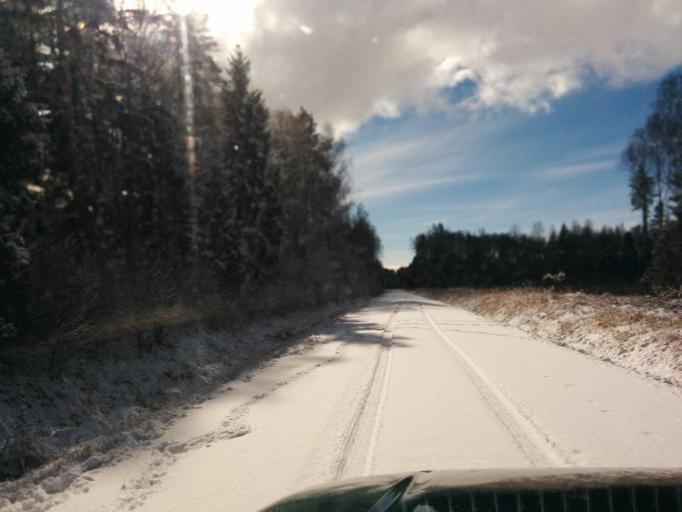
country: LV
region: Jelgava
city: Jelgava
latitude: 56.6189
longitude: 23.6459
